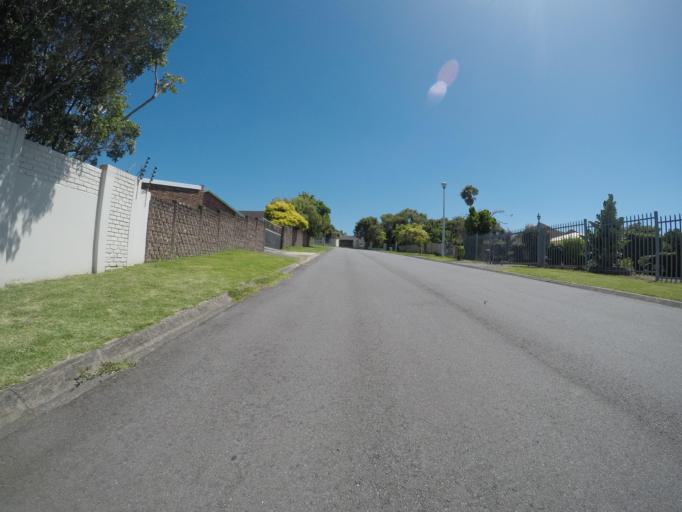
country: ZA
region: Eastern Cape
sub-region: Buffalo City Metropolitan Municipality
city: East London
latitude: -32.9707
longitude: 27.9449
